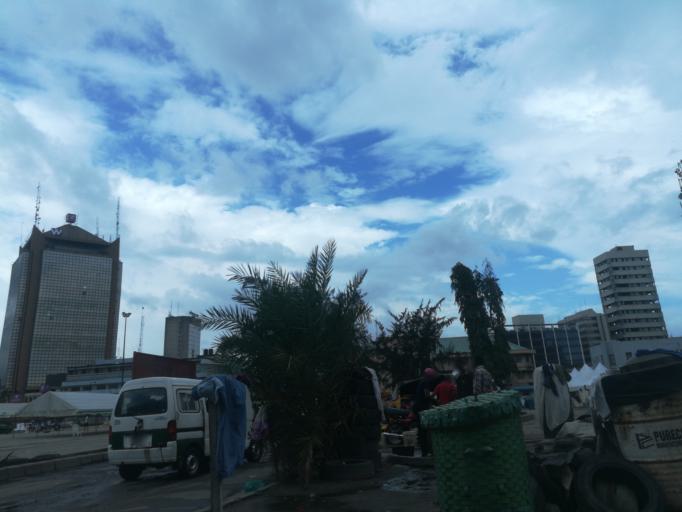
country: NG
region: Lagos
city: Lagos
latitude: 6.4532
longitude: 3.3841
